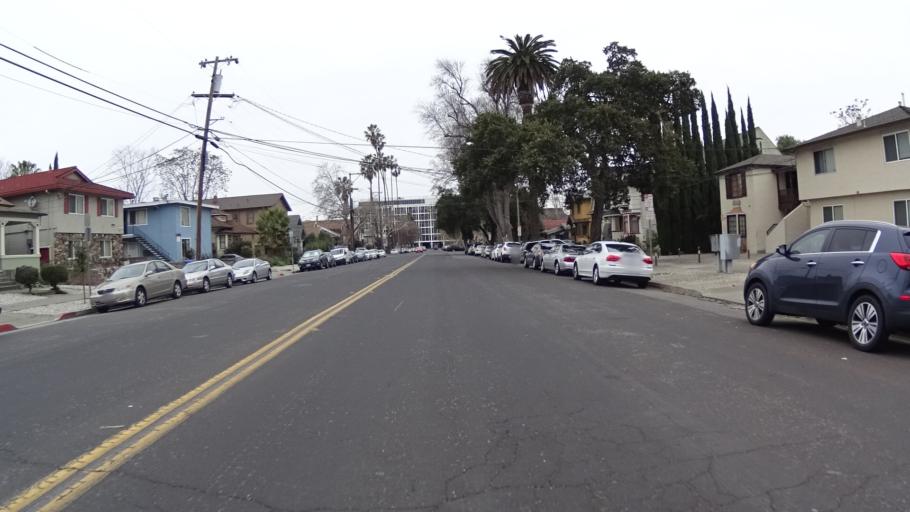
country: US
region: California
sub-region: Santa Clara County
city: San Jose
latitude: 37.3296
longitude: -121.8800
